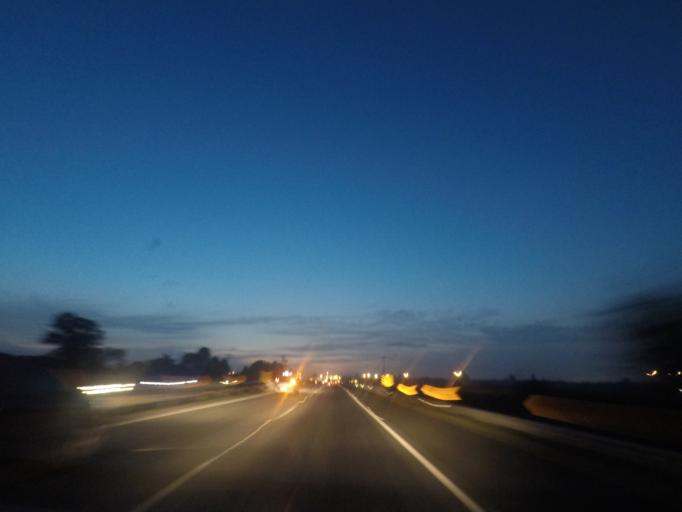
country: BR
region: Parana
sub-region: Pinhais
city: Pinhais
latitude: -25.4878
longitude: -49.1811
